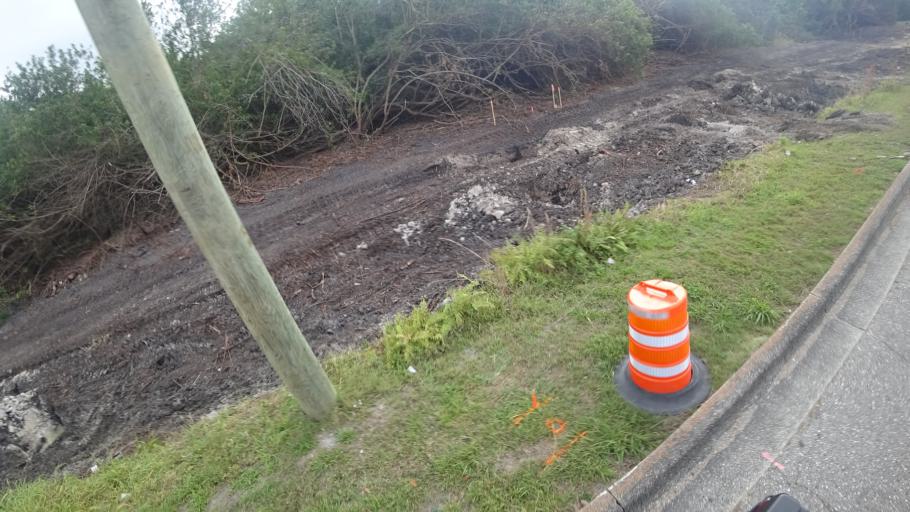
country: US
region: Florida
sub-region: Manatee County
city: Samoset
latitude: 27.4585
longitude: -82.5056
